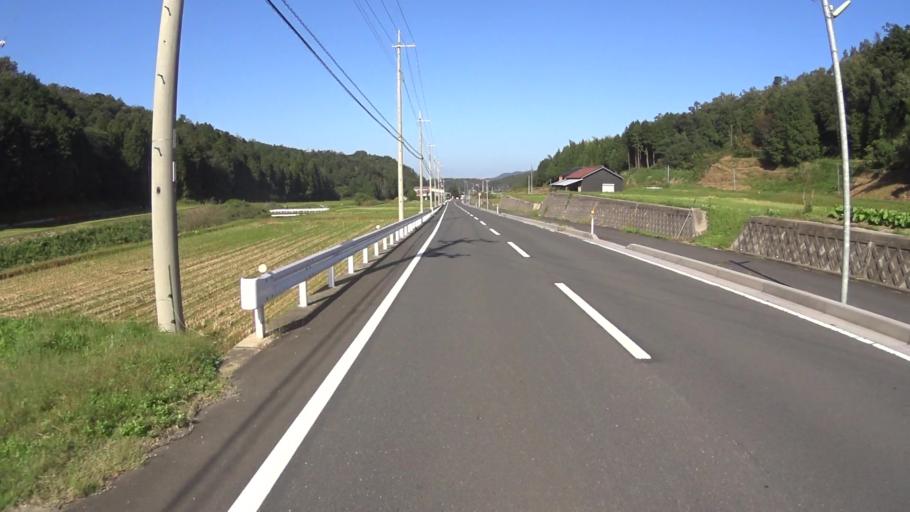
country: JP
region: Kyoto
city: Miyazu
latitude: 35.6510
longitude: 135.1215
